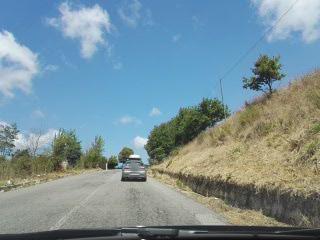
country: IT
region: Calabria
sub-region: Provincia di Vibo-Valentia
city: Spilinga
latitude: 38.6193
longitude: 15.8896
